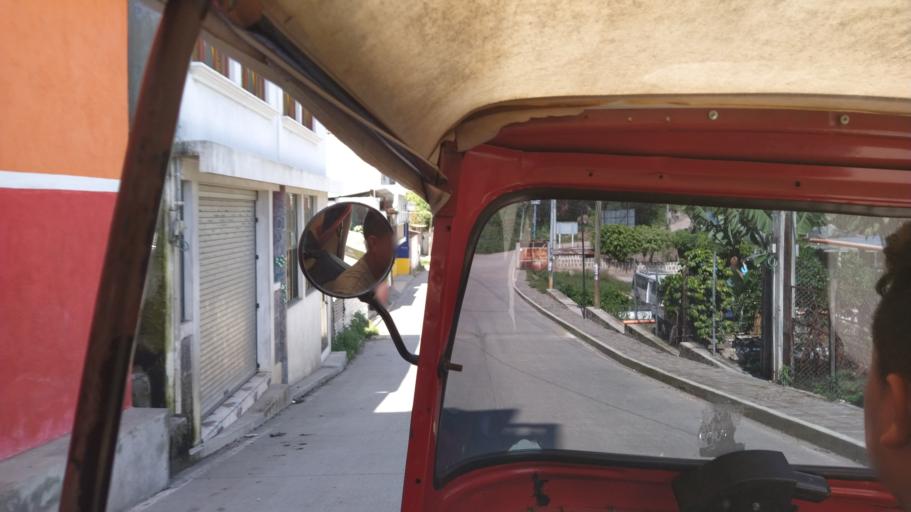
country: GT
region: Solola
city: San Pedro La Laguna
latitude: 14.6925
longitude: -91.2770
